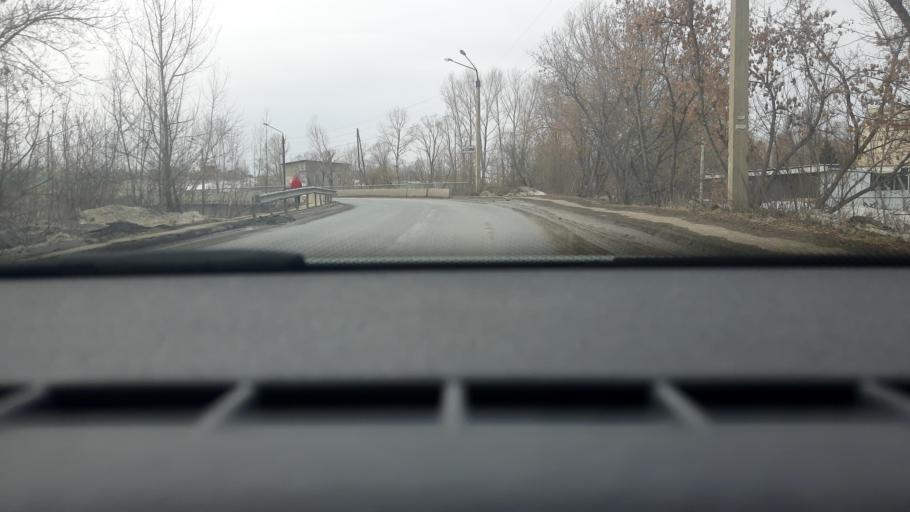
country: RU
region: Chelyabinsk
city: Asha
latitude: 54.9963
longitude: 57.2613
